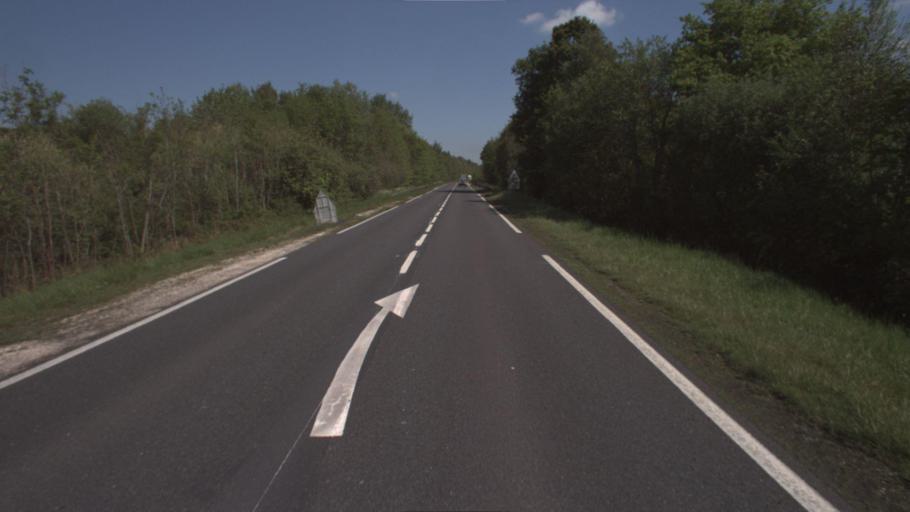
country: FR
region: Ile-de-France
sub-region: Departement de Seine-et-Marne
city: Chaumes-en-Brie
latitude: 48.6814
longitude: 2.8147
